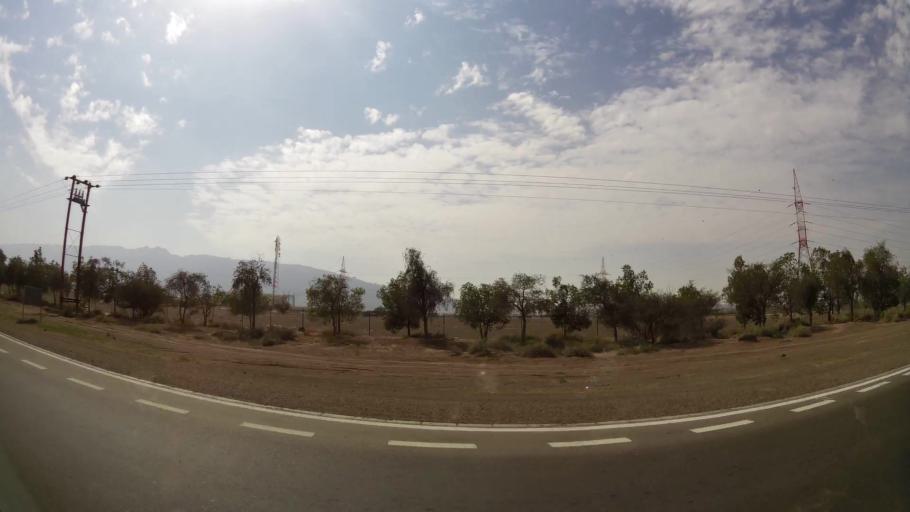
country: AE
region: Abu Dhabi
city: Al Ain
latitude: 24.1136
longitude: 55.8247
